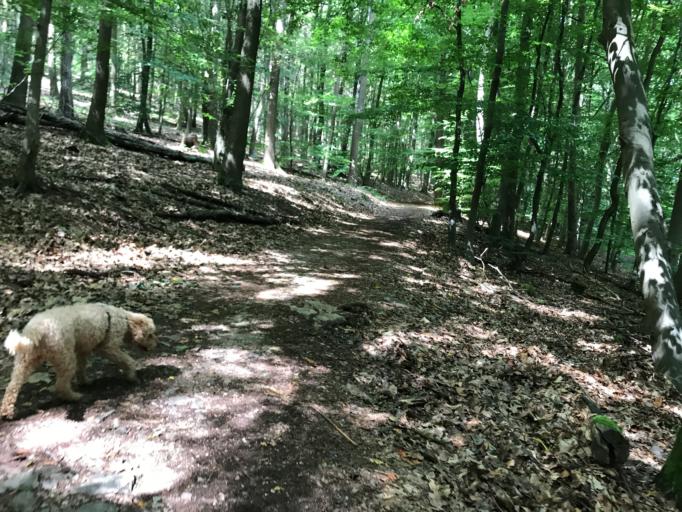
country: DE
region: Rheinland-Pfalz
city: Weiler
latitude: 49.9706
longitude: 7.8679
